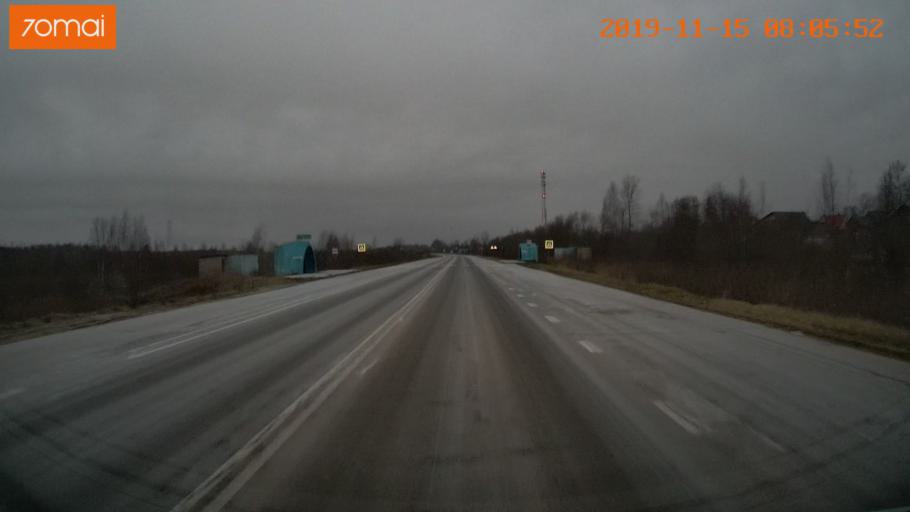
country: RU
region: Vologda
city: Cherepovets
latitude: 59.0191
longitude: 38.0494
